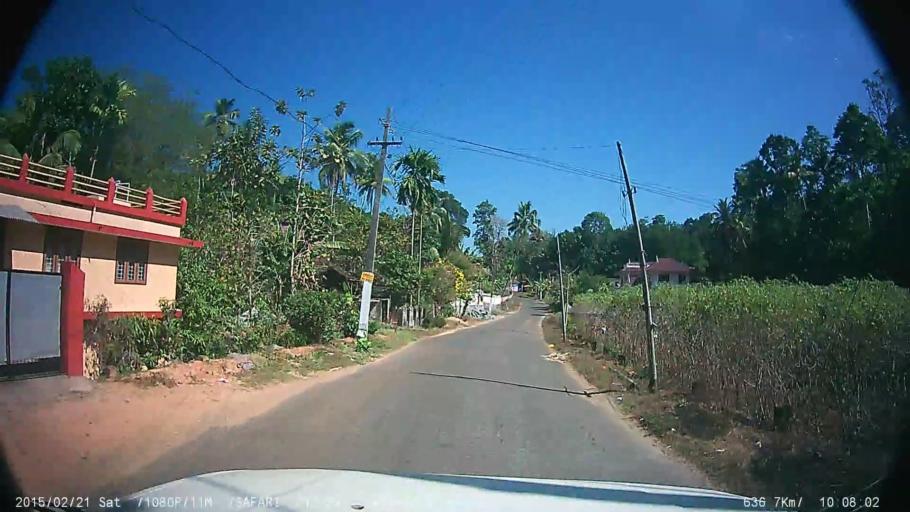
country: IN
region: Kerala
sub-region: Ernakulam
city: Piravam
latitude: 9.8763
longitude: 76.6062
